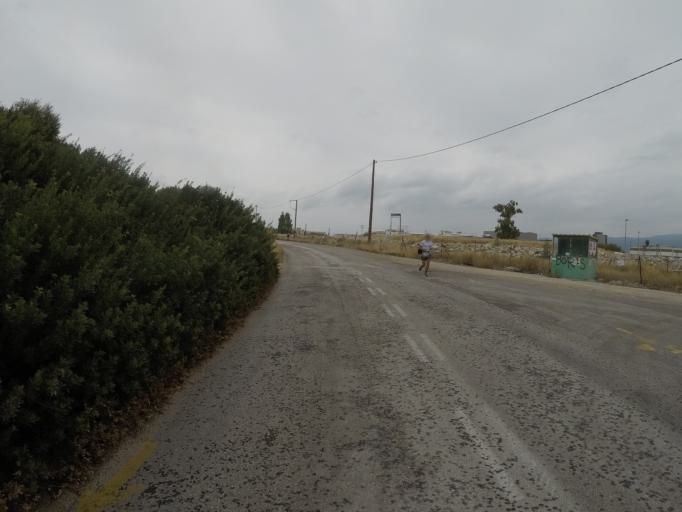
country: GR
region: Peloponnese
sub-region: Nomos Korinthias
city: Isthmia
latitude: 37.9201
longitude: 23.0576
